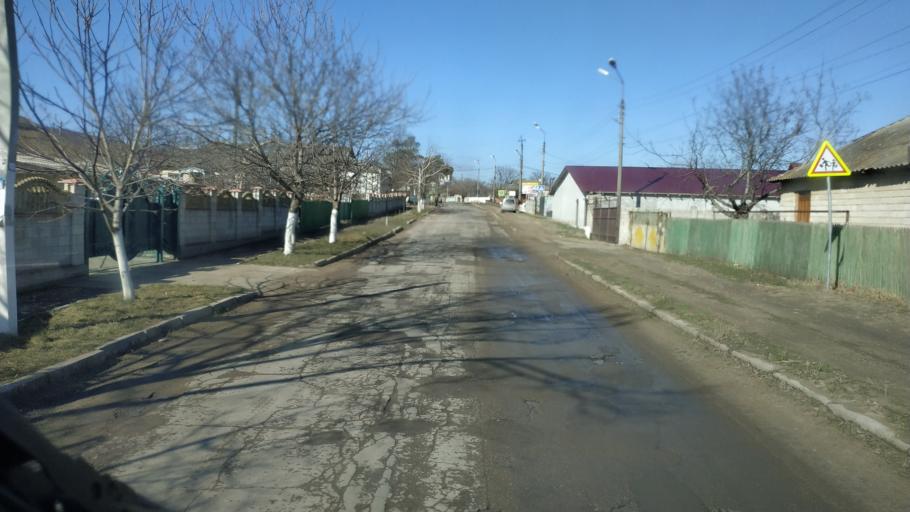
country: MD
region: Hincesti
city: Hincesti
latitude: 46.9711
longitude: 28.5860
